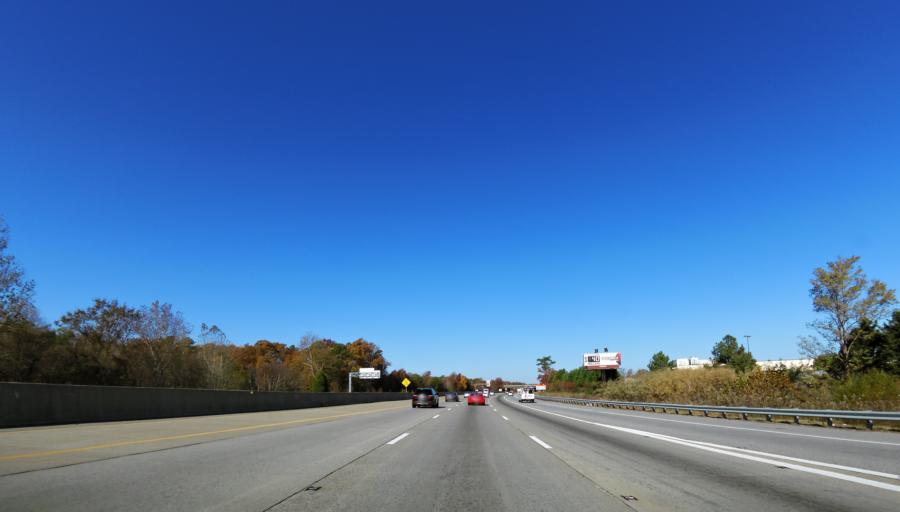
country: US
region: Virginia
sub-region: York County
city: Yorktown
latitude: 37.1205
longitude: -76.5132
